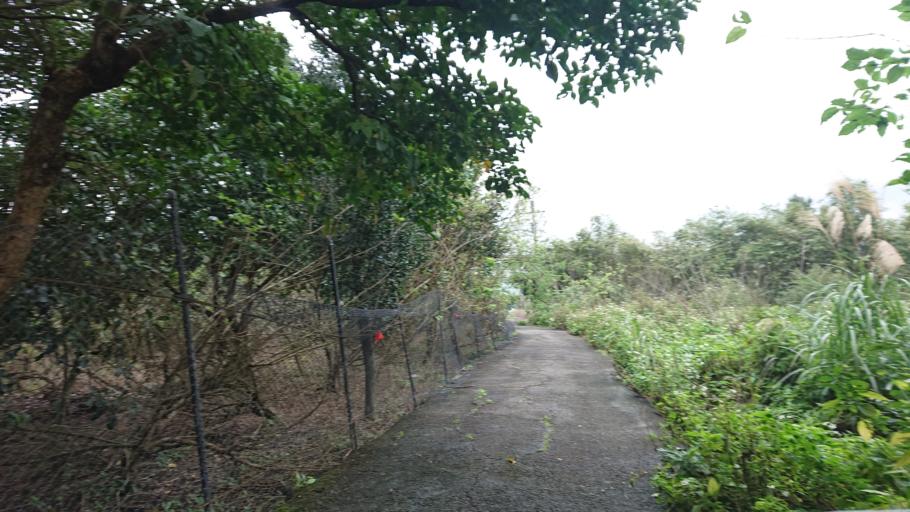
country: TW
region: Taiwan
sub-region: Taoyuan
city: Taoyuan
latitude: 24.9372
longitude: 121.3863
